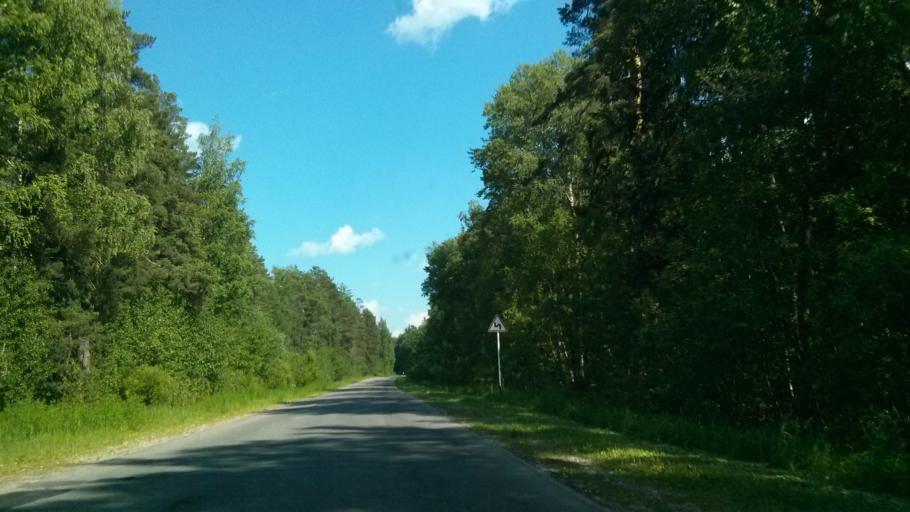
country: RU
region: Vladimir
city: Melenki
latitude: 55.3331
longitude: 41.6807
